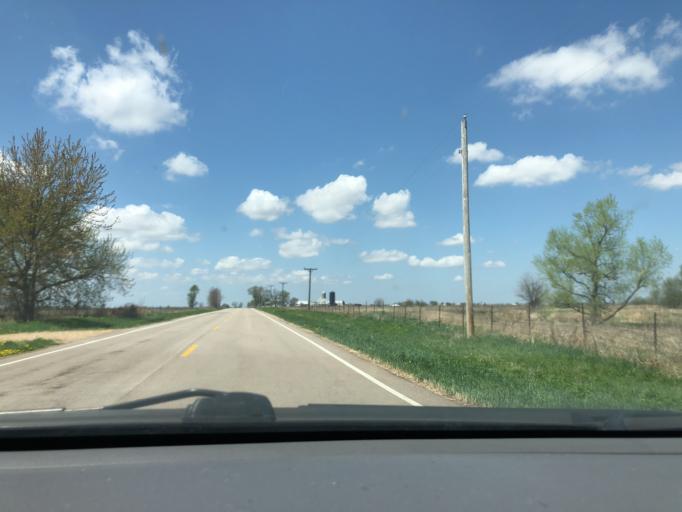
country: US
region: Illinois
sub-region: Kane County
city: Hampshire
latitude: 42.1100
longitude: -88.5743
